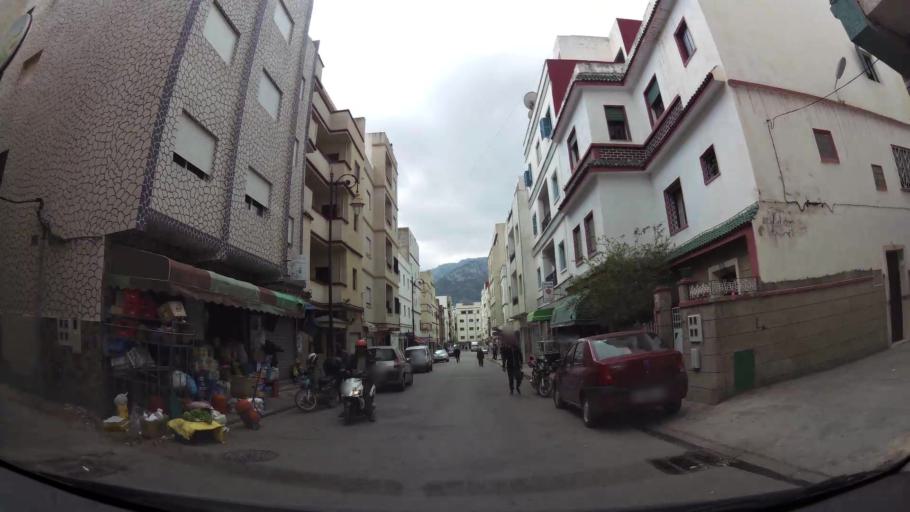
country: MA
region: Tanger-Tetouan
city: Tetouan
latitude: 35.5645
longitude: -5.3673
